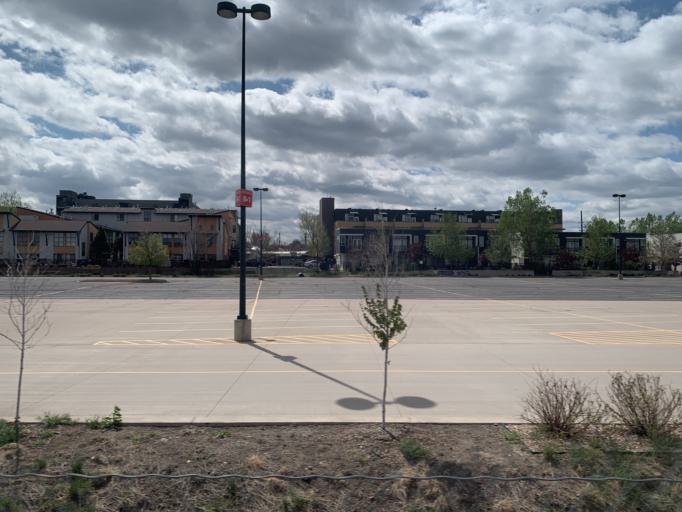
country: US
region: Colorado
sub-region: Denver County
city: Denver
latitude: 39.7659
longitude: -104.9818
